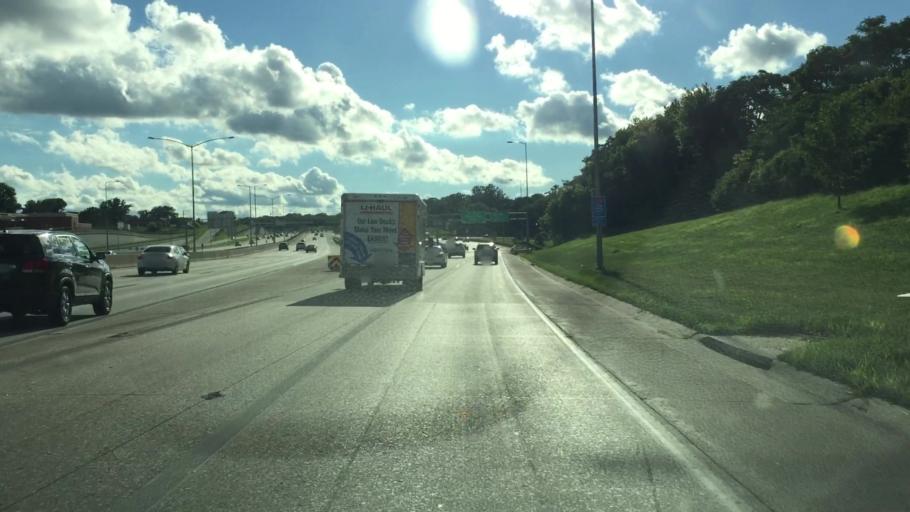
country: US
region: Iowa
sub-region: Polk County
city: Des Moines
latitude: 41.5962
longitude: -93.6334
